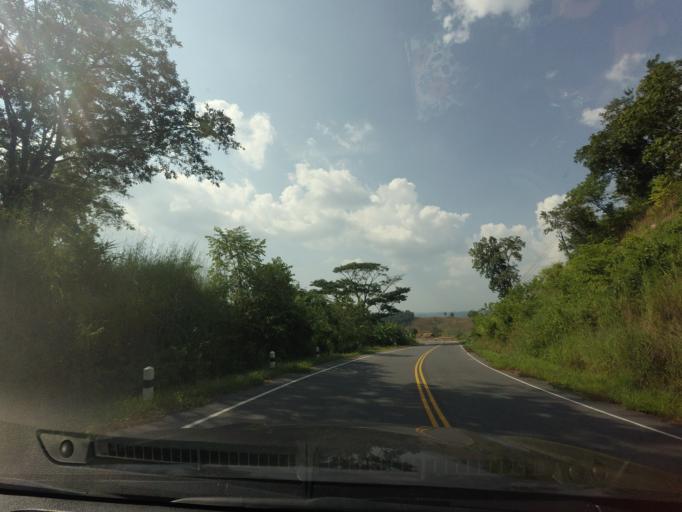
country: TH
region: Nan
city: Santi Suk
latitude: 18.9814
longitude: 100.9517
